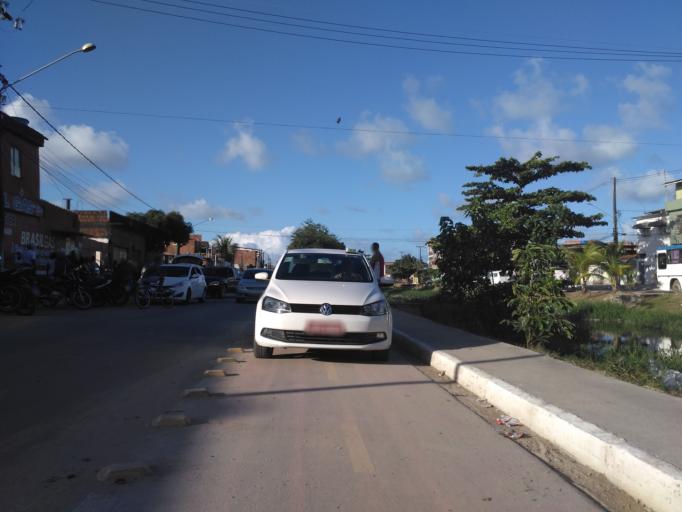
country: BR
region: Pernambuco
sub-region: Jaboatao Dos Guararapes
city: Jaboatao
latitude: -8.1847
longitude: -34.9388
